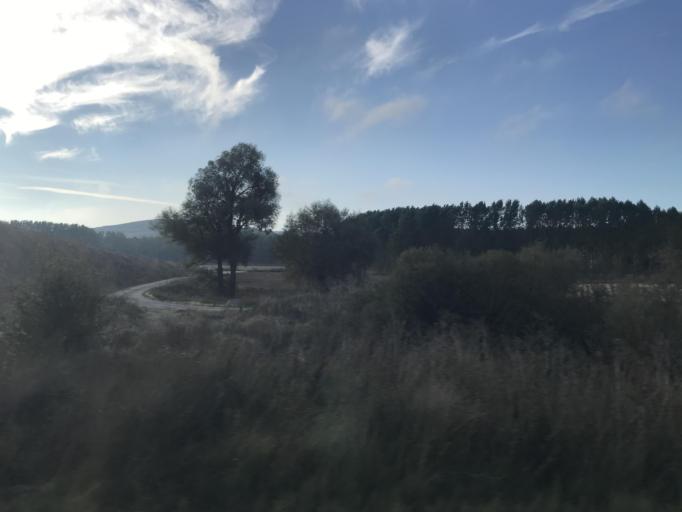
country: ES
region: Castille and Leon
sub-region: Provincia de Burgos
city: Celada del Camino
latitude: 42.2590
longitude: -3.9285
